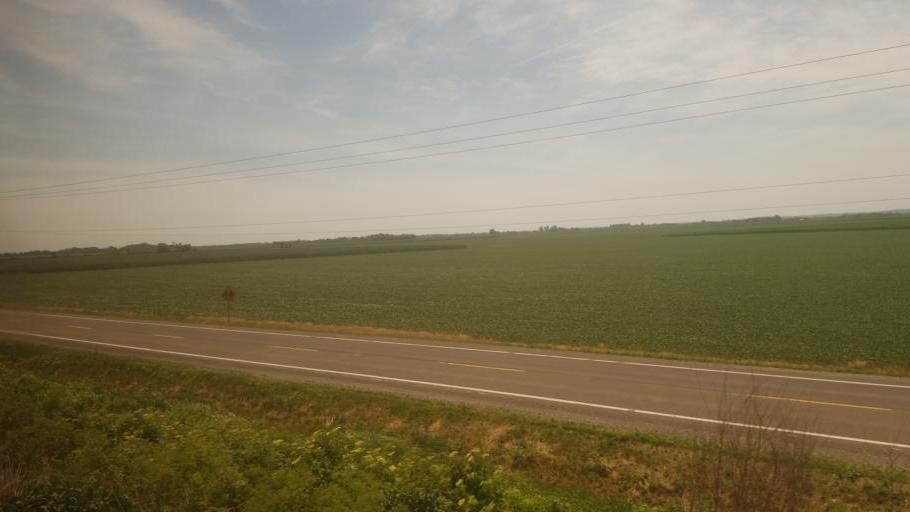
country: US
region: Missouri
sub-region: Carroll County
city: Carrollton
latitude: 39.3097
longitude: -93.6478
